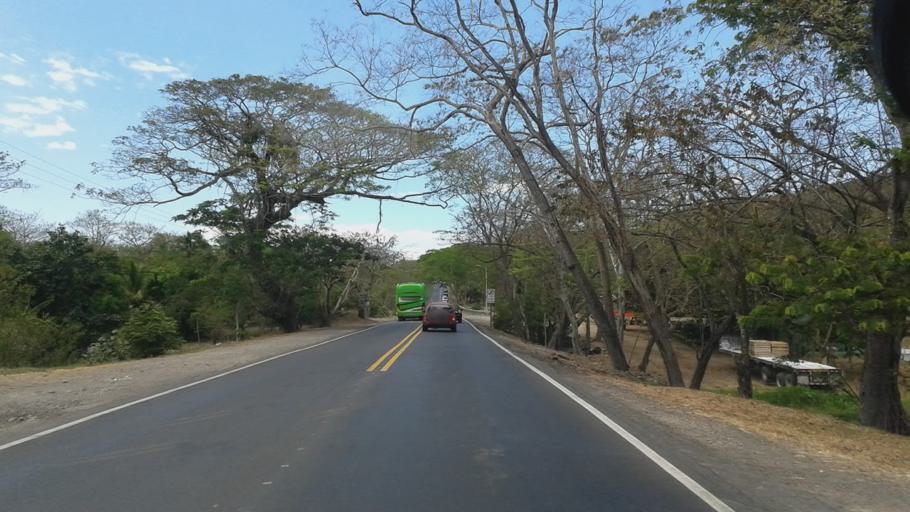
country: CR
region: Guanacaste
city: Juntas
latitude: 10.1344
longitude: -84.9044
